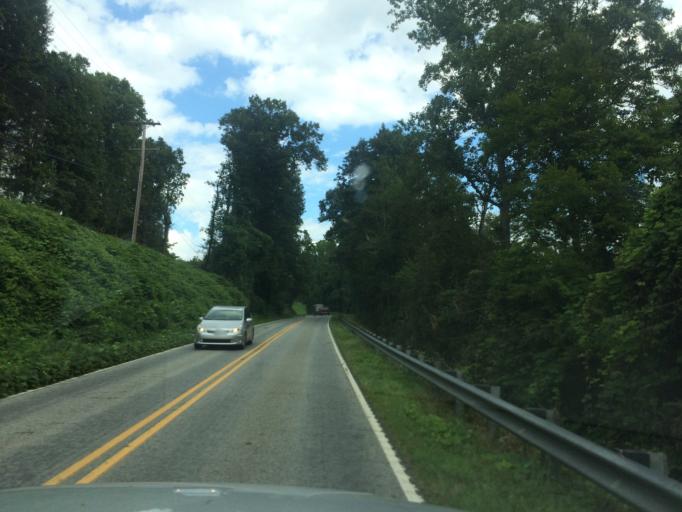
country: US
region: North Carolina
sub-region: Polk County
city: Columbus
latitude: 35.3391
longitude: -82.1826
